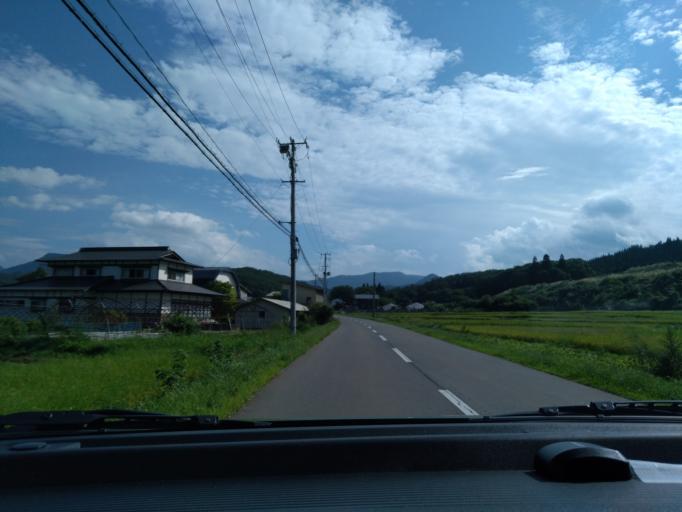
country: JP
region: Iwate
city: Shizukuishi
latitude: 39.6509
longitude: 140.9928
